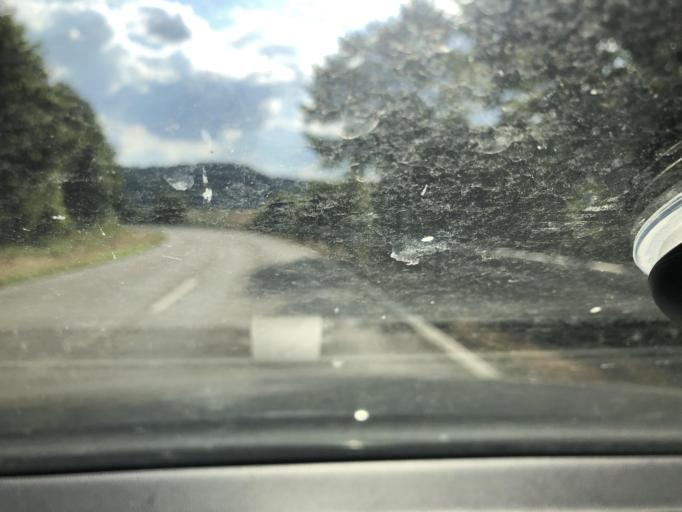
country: DE
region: Baden-Wuerttemberg
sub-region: Tuebingen Region
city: Trochtelfingen
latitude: 48.3643
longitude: 9.2099
